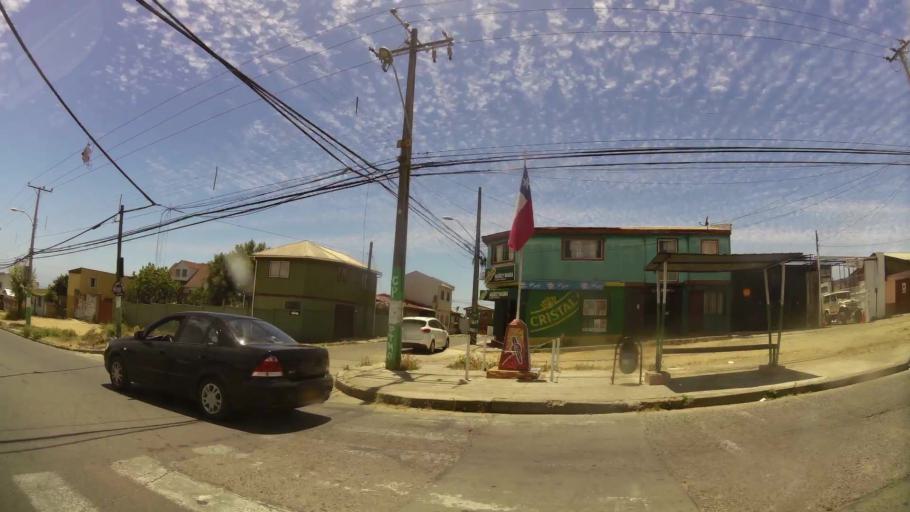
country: CL
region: Valparaiso
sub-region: Provincia de Valparaiso
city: Vina del Mar
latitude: -33.0473
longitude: -71.5820
